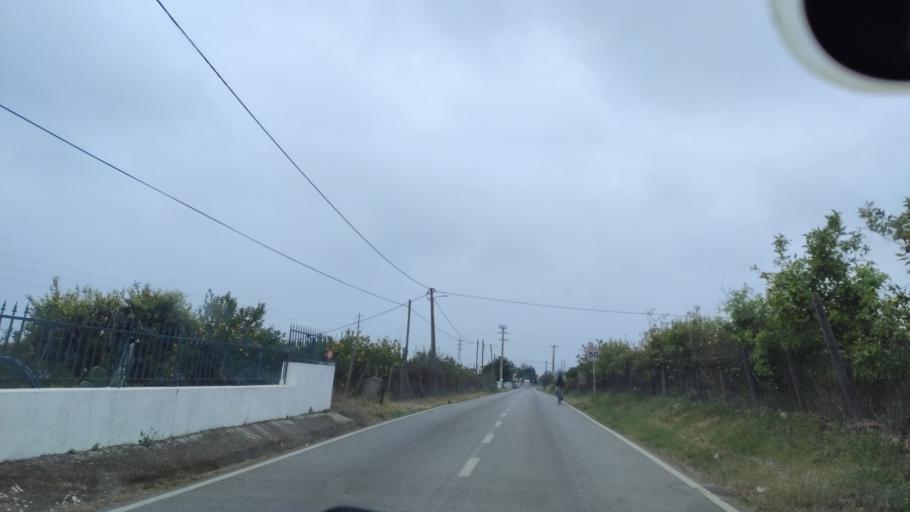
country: PT
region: Faro
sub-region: Faro
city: Santa Barbara de Nexe
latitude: 37.0740
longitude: -7.9489
